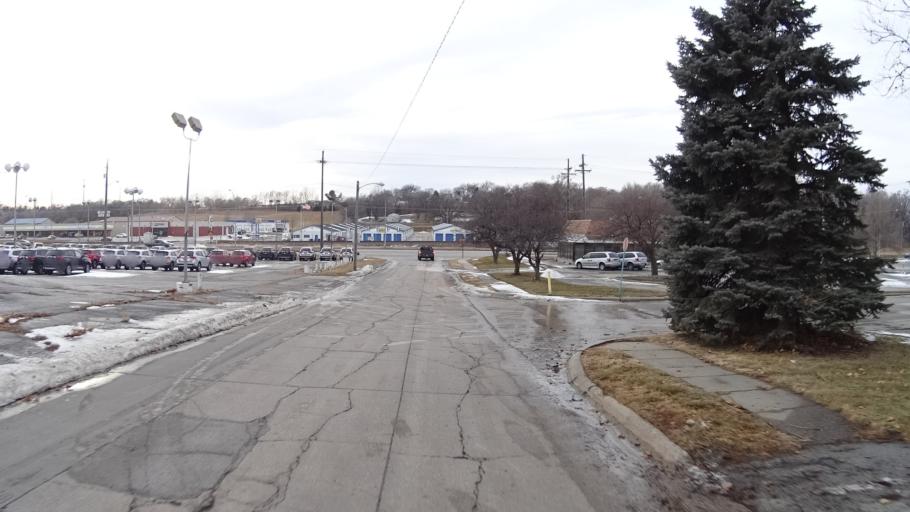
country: US
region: Nebraska
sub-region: Sarpy County
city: Bellevue
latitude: 41.1733
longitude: -95.9245
